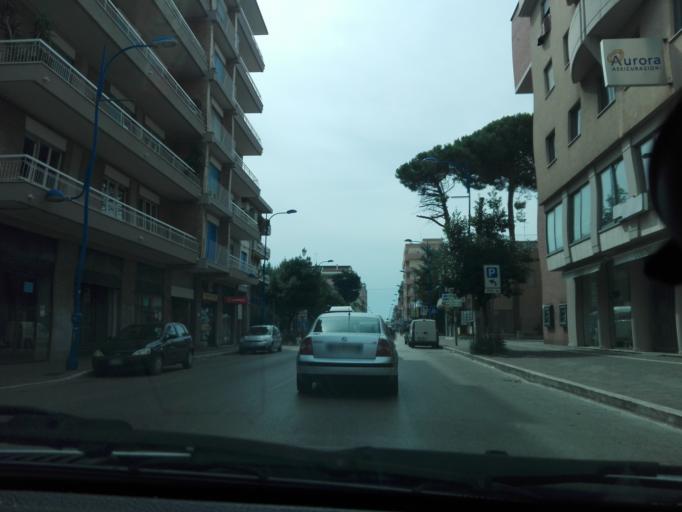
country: IT
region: Abruzzo
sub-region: Provincia di Pescara
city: Montesilvano Marina
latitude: 42.5146
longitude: 14.1520
